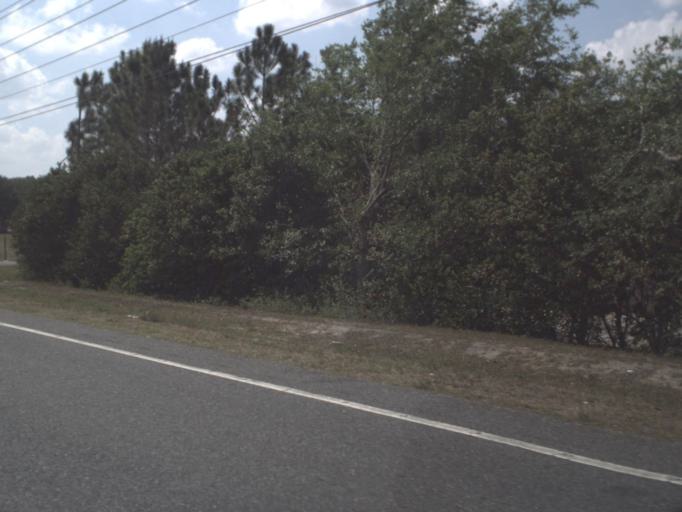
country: US
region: Florida
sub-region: Lake County
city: Groveland
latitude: 28.6372
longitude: -81.8132
